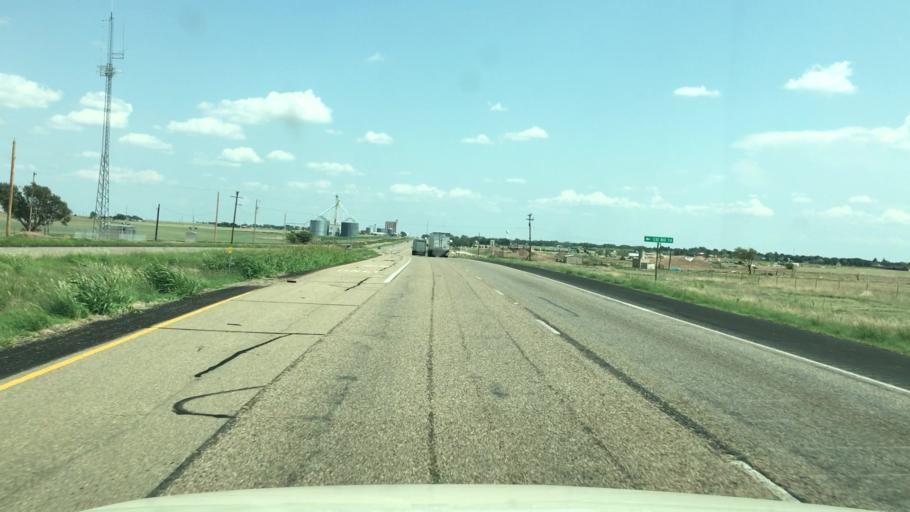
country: US
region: Texas
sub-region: Armstrong County
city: Claude
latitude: 35.1208
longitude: -101.3851
